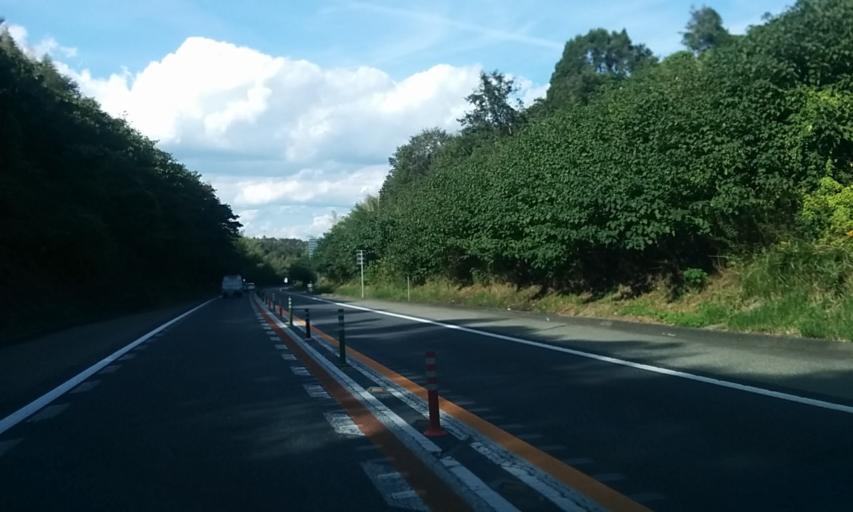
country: JP
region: Kyoto
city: Tanabe
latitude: 34.8132
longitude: 135.7521
